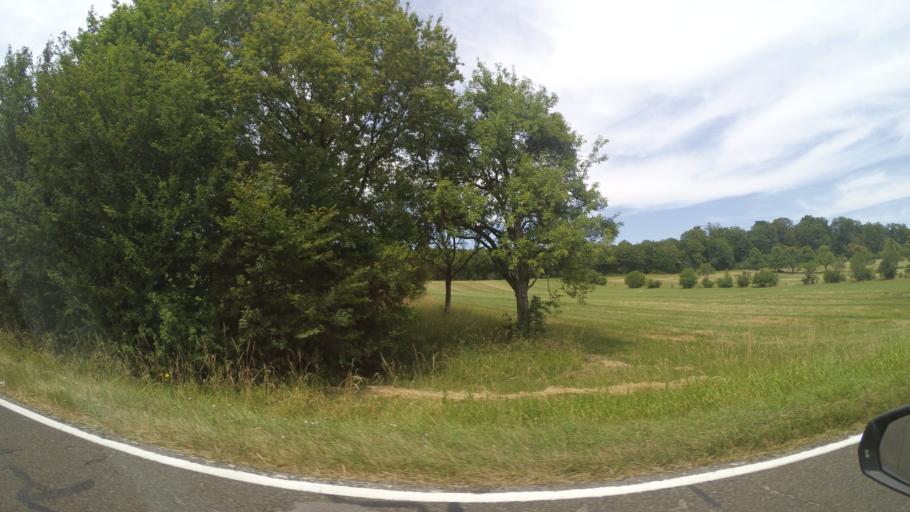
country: DE
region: Saarland
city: Mettlach
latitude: 49.4165
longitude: 6.5539
